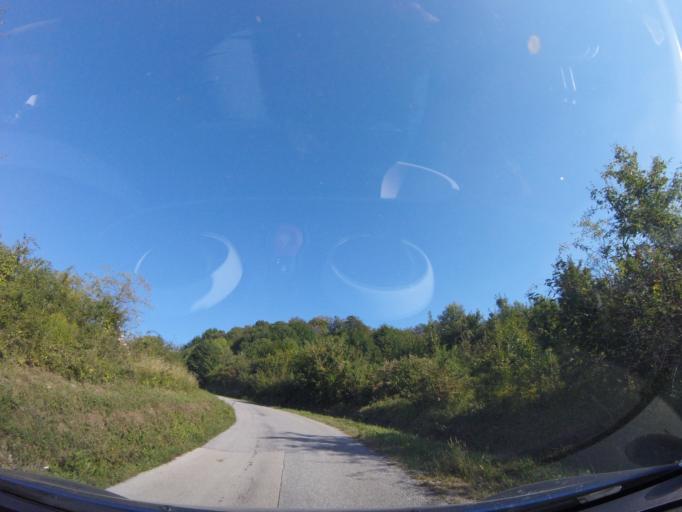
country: HR
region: Zagrebacka
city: Rude
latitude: 45.7559
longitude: 15.6658
